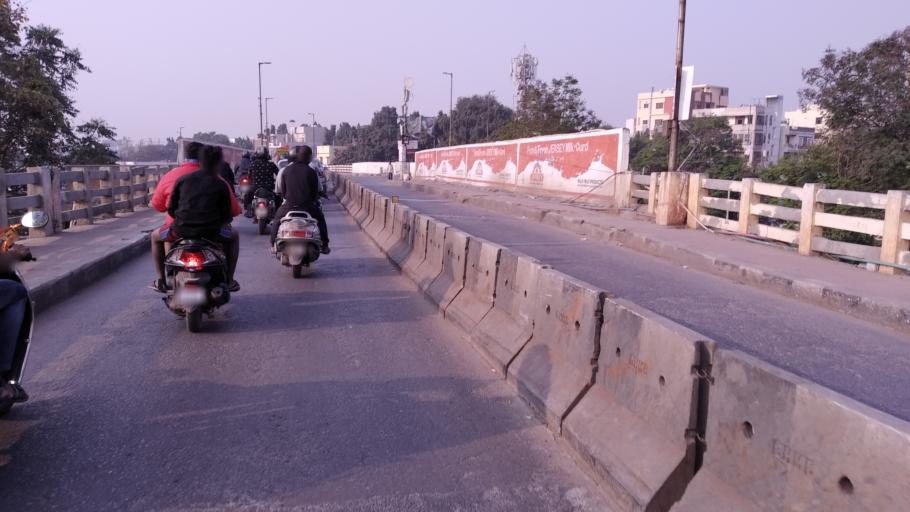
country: IN
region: Telangana
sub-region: Rangareddi
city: Quthbullapur
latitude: 17.4556
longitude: 78.4504
